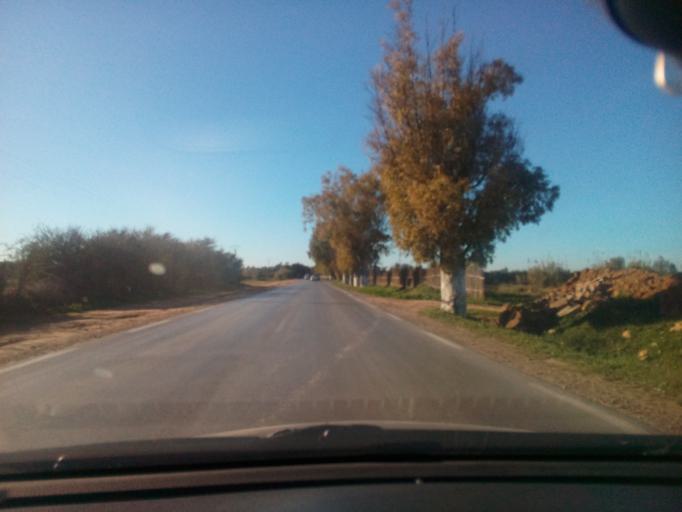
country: DZ
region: Mostaganem
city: Mostaganem
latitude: 35.9006
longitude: 0.2224
